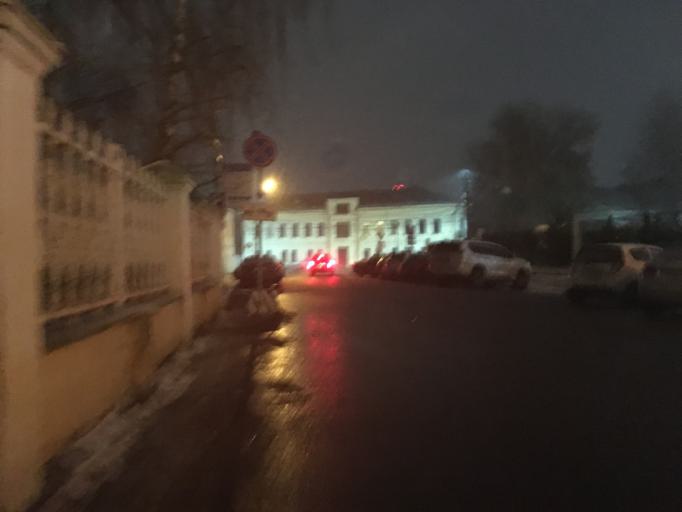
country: RU
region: Tula
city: Tula
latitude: 54.1964
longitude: 37.6169
